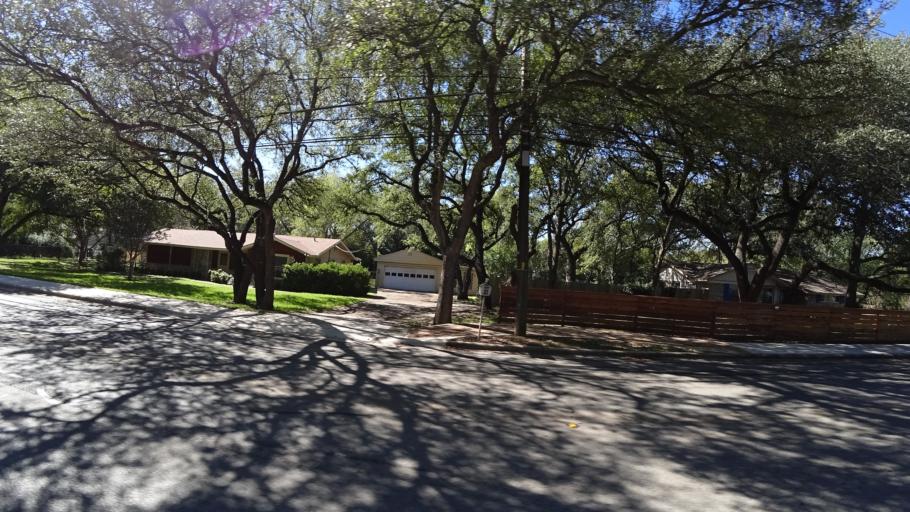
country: US
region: Texas
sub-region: Travis County
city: Rollingwood
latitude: 30.2266
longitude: -97.8058
